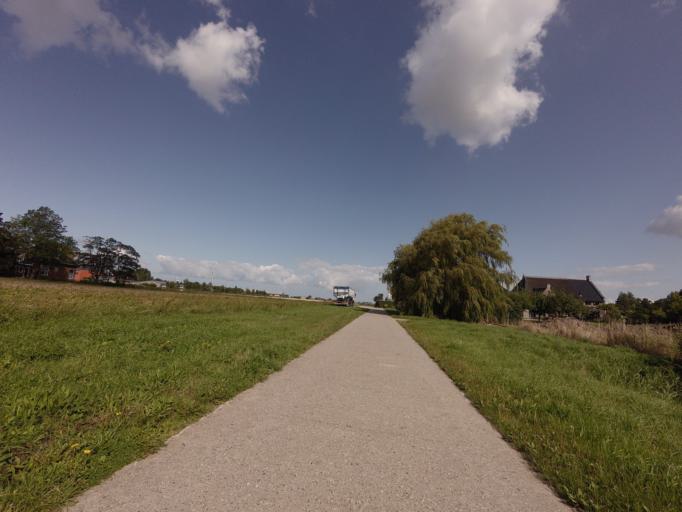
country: NL
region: Friesland
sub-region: Gemeente Het Bildt
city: Sint Jacobiparochie
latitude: 53.2726
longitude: 5.6155
